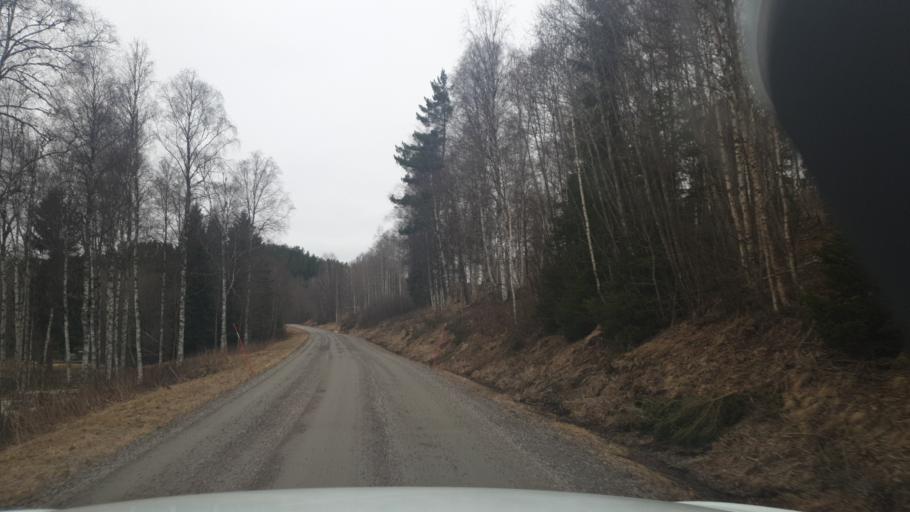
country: NO
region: Ostfold
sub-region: Romskog
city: Romskog
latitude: 59.6800
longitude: 11.9330
